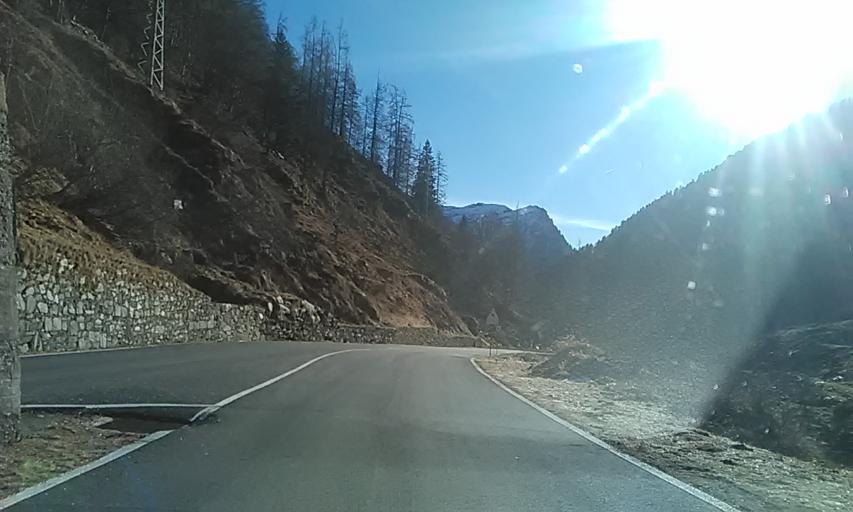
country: IT
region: Piedmont
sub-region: Provincia di Vercelli
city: Carcoforo
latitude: 45.9019
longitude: 8.0562
